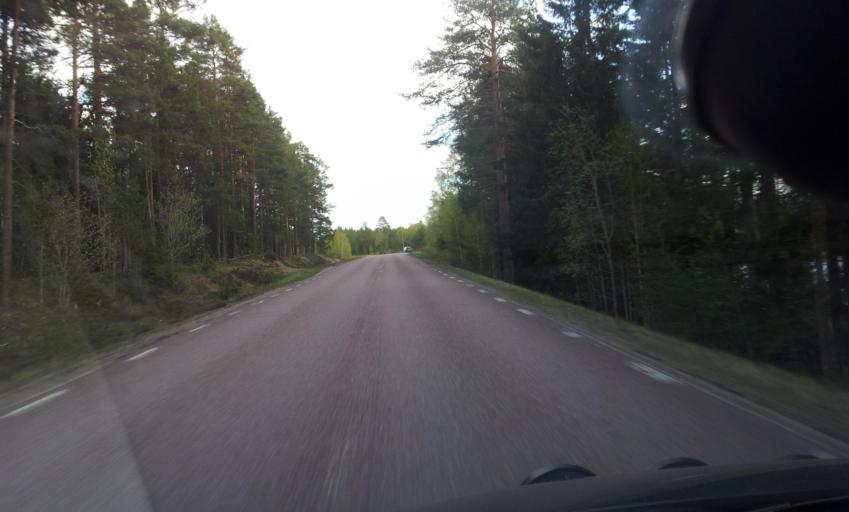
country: SE
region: Gaevleborg
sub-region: Bollnas Kommun
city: Kilafors
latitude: 61.3847
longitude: 16.6139
